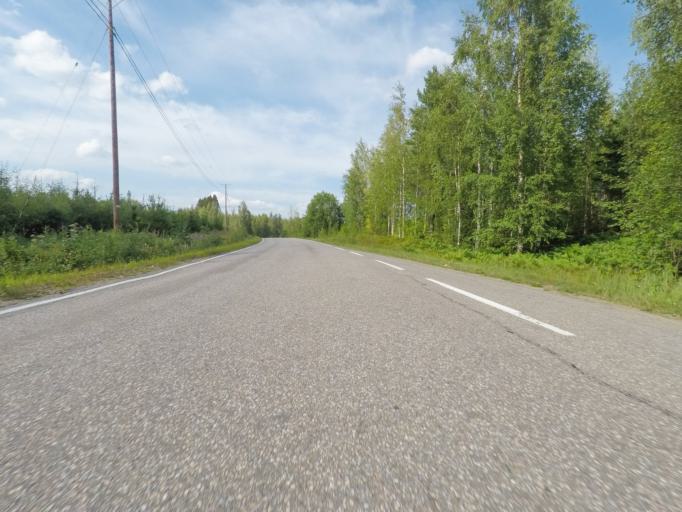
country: FI
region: Southern Savonia
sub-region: Savonlinna
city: Sulkava
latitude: 61.7562
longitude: 28.2275
